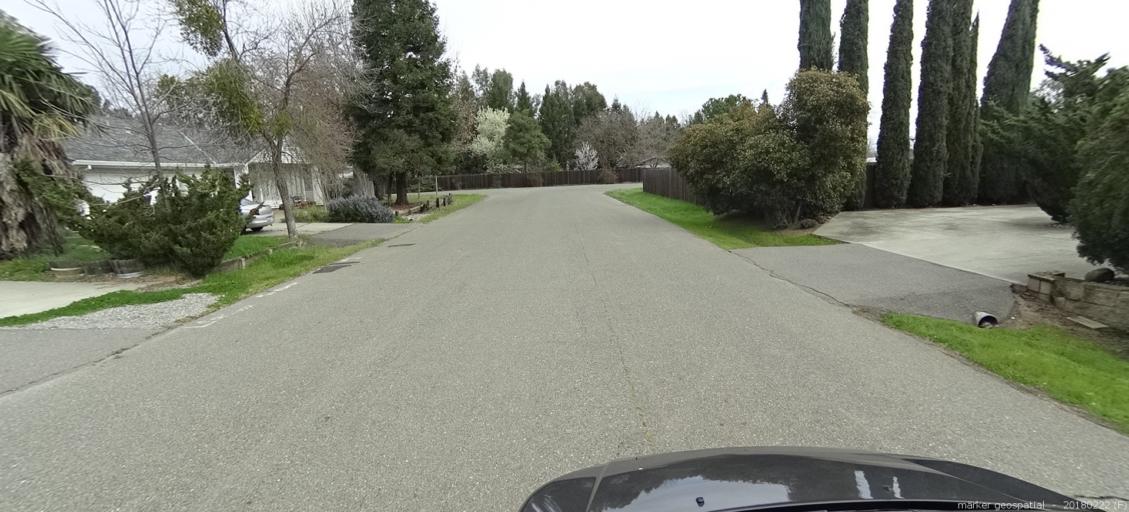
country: US
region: California
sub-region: Sacramento County
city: Rio Linda
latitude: 38.7179
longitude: -121.4143
